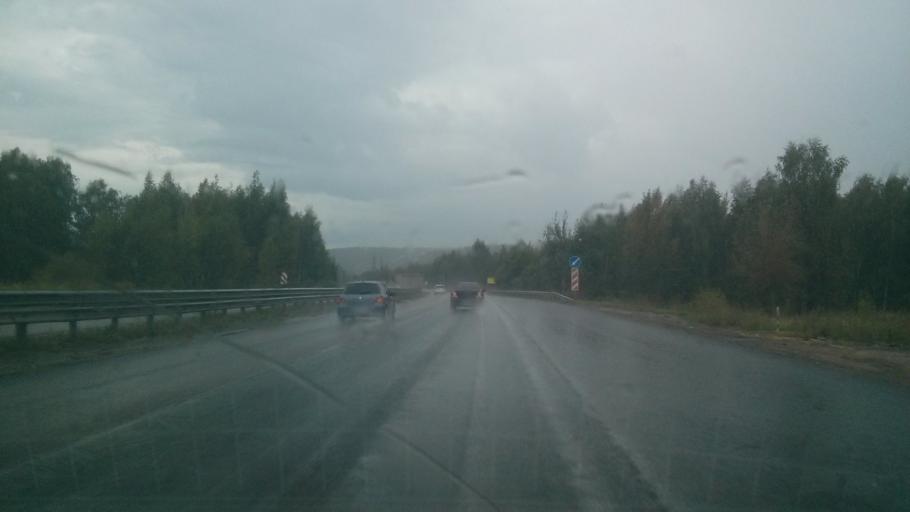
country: RU
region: Nizjnij Novgorod
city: Afonino
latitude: 56.2305
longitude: 44.0712
